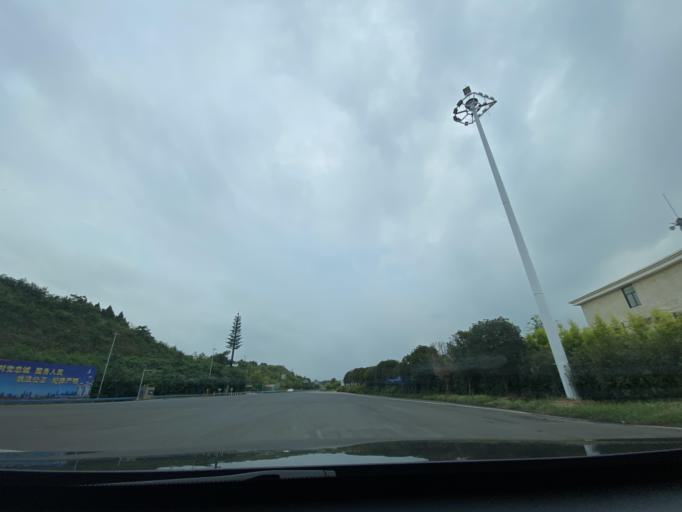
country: CN
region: Sichuan
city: Jiancheng
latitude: 30.4989
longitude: 104.4475
